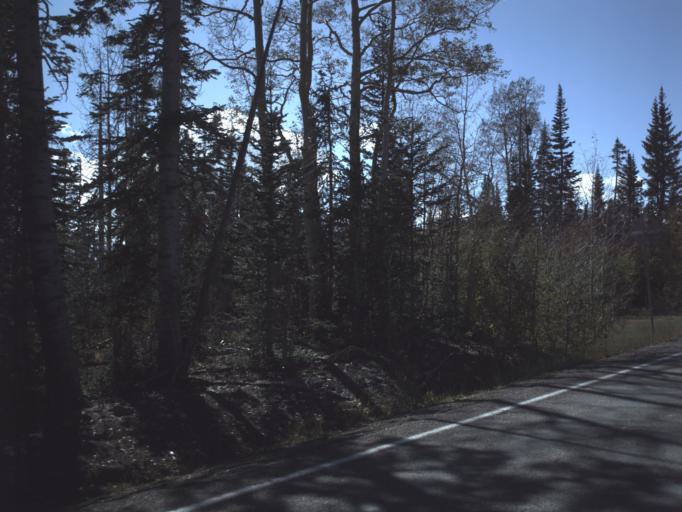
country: US
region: Utah
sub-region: Iron County
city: Parowan
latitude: 37.6543
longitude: -112.8086
